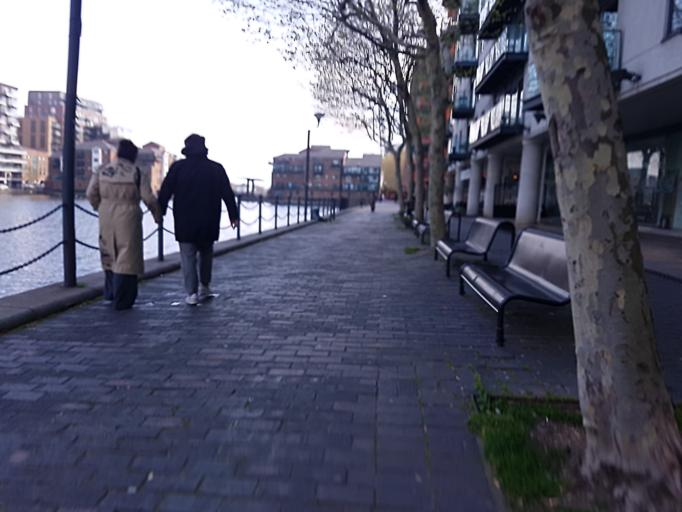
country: GB
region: England
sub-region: Greater London
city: Poplar
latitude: 51.4981
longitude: -0.0174
